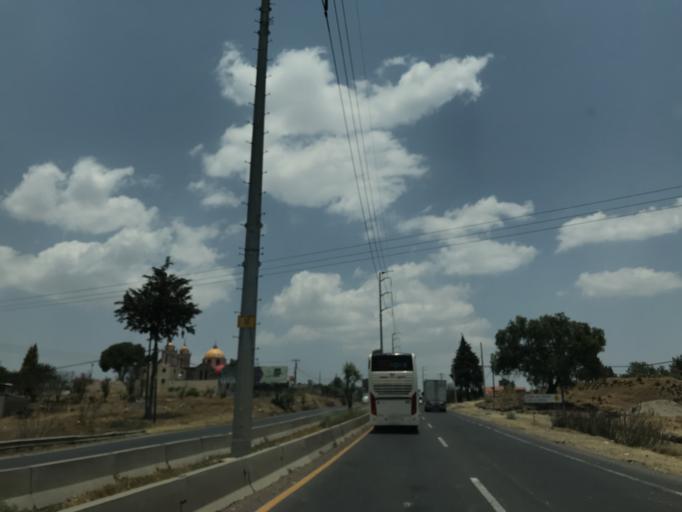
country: MX
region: Tlaxcala
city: Yauhquemehcan
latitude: 19.4052
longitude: -98.1711
